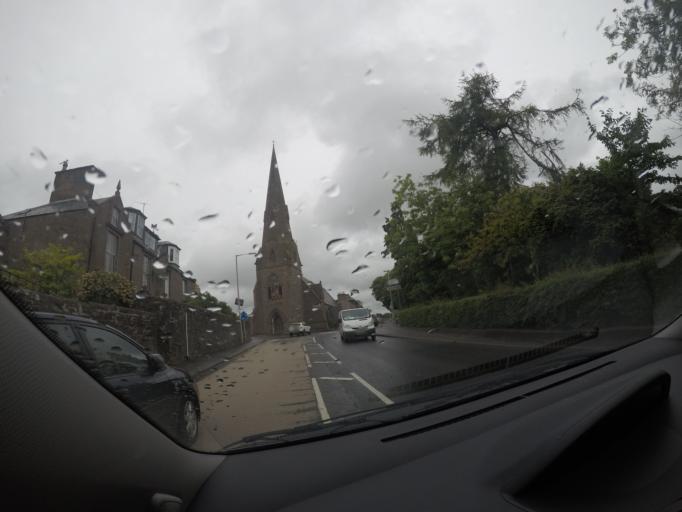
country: GB
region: Scotland
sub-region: Angus
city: Brechin
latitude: 56.7335
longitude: -2.6560
